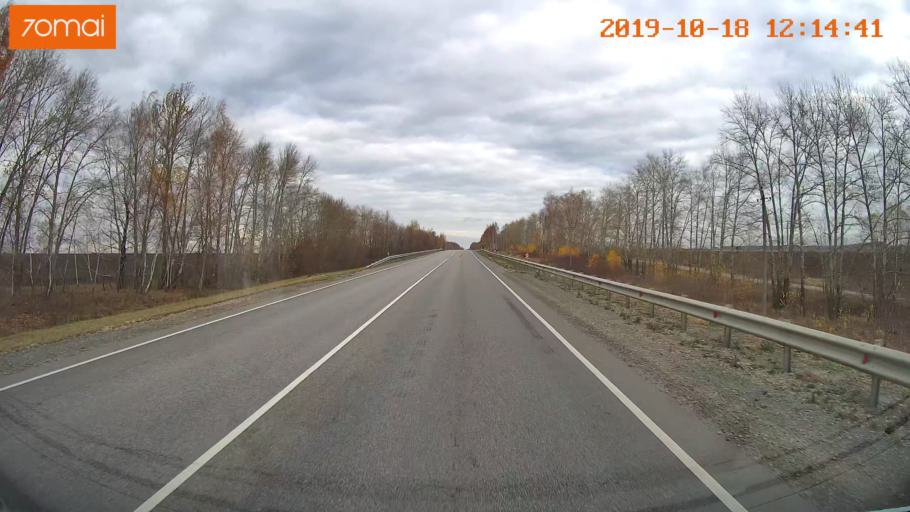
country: RU
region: Rjazan
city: Zakharovo
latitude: 54.4338
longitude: 39.3873
